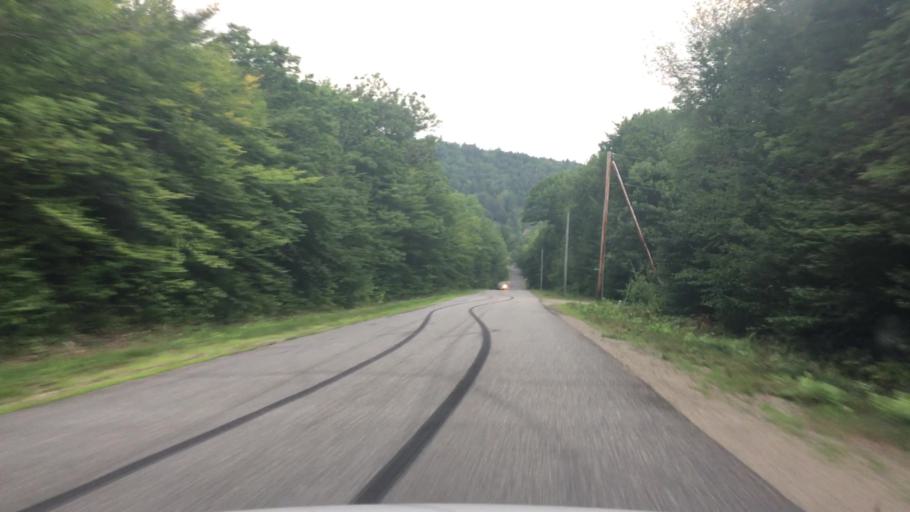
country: US
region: Maine
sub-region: Knox County
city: Washington
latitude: 44.3706
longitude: -69.3461
